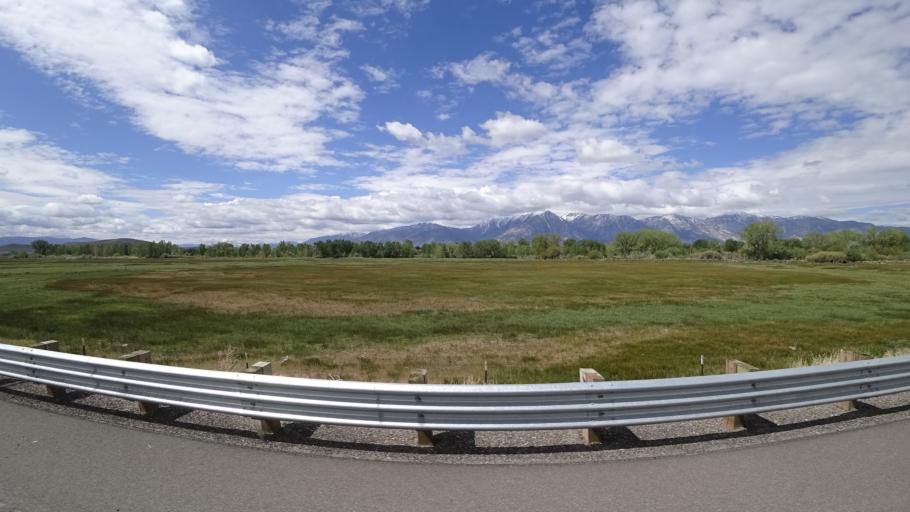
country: US
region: Nevada
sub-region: Douglas County
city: Gardnerville Ranchos
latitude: 38.9121
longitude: -119.7120
